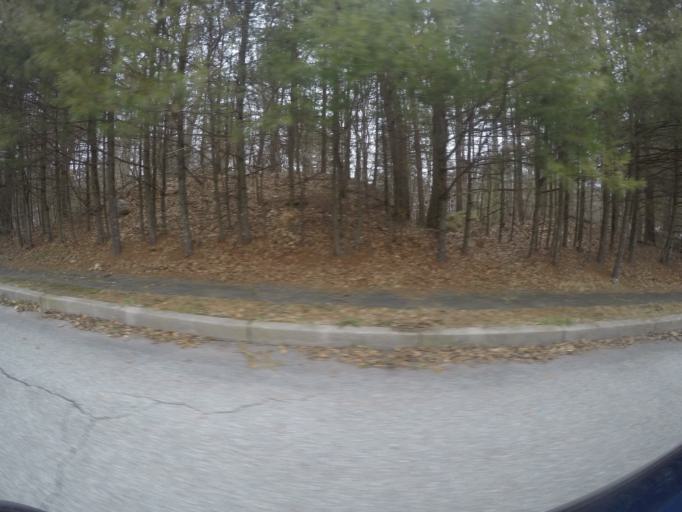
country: US
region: Massachusetts
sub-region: Bristol County
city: Easton
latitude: 42.0598
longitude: -71.1442
